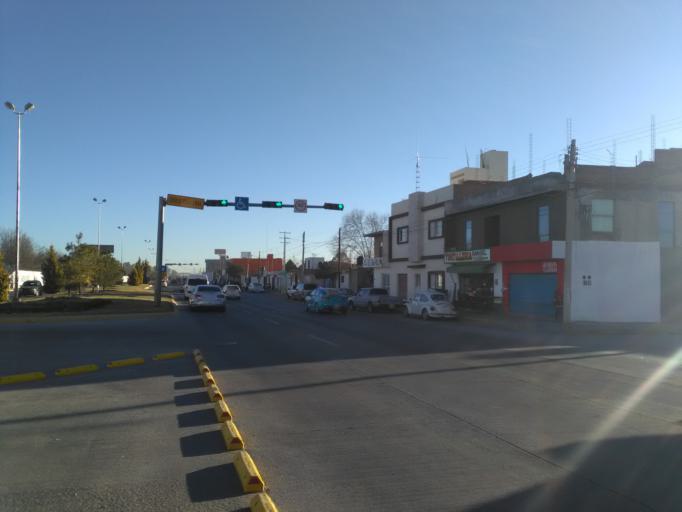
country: MX
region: Durango
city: Victoria de Durango
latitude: 24.0563
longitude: -104.6396
